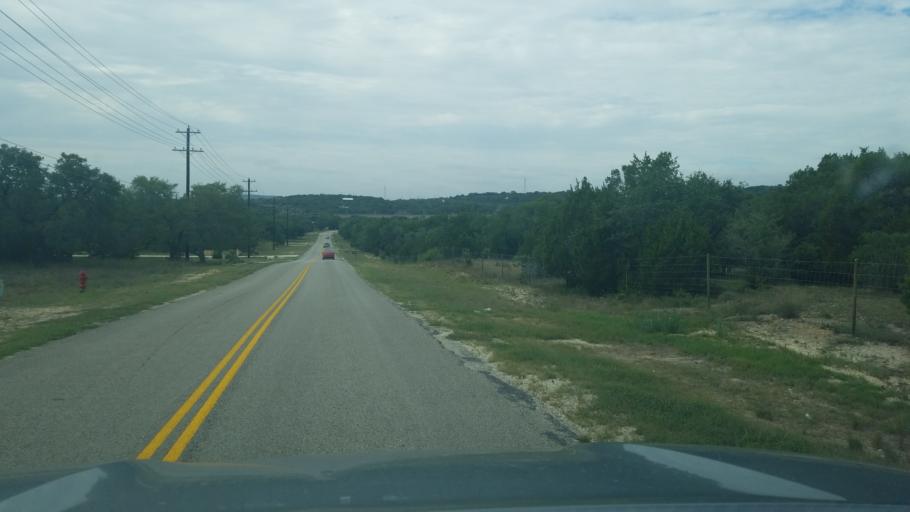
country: US
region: Texas
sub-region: Comal County
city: Bulverde
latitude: 29.7929
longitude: -98.4110
